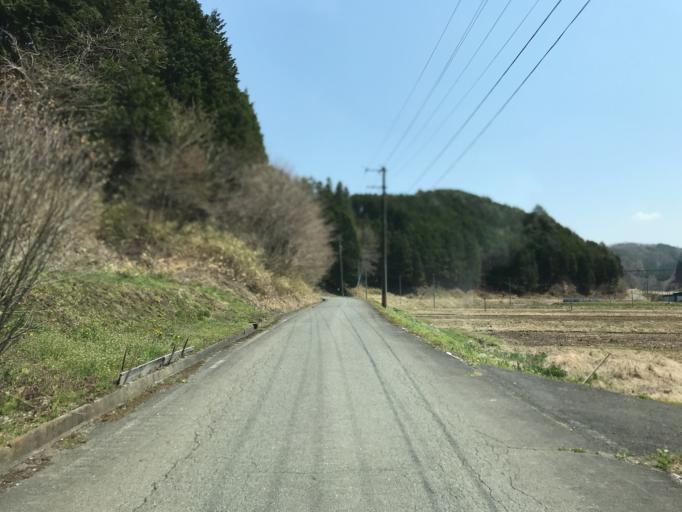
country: JP
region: Fukushima
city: Ishikawa
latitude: 36.9939
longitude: 140.5885
